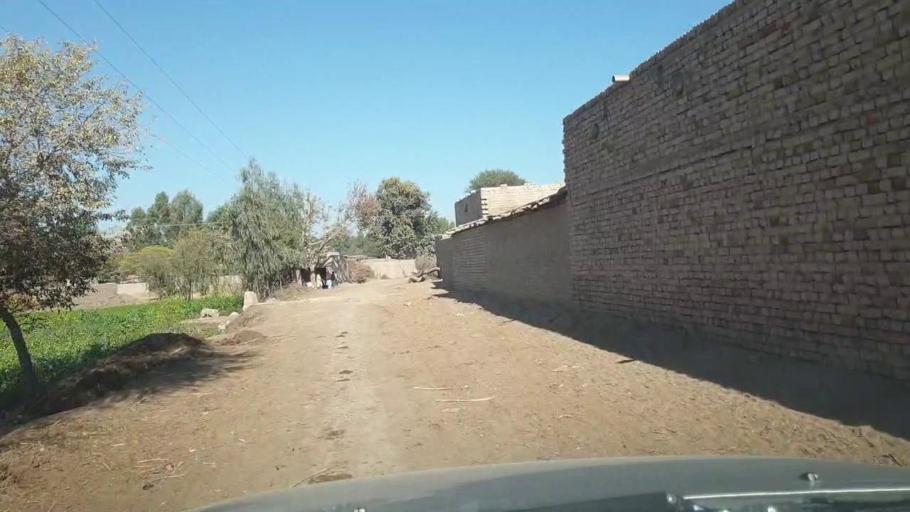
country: PK
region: Sindh
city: Ghotki
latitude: 28.1008
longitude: 69.3419
